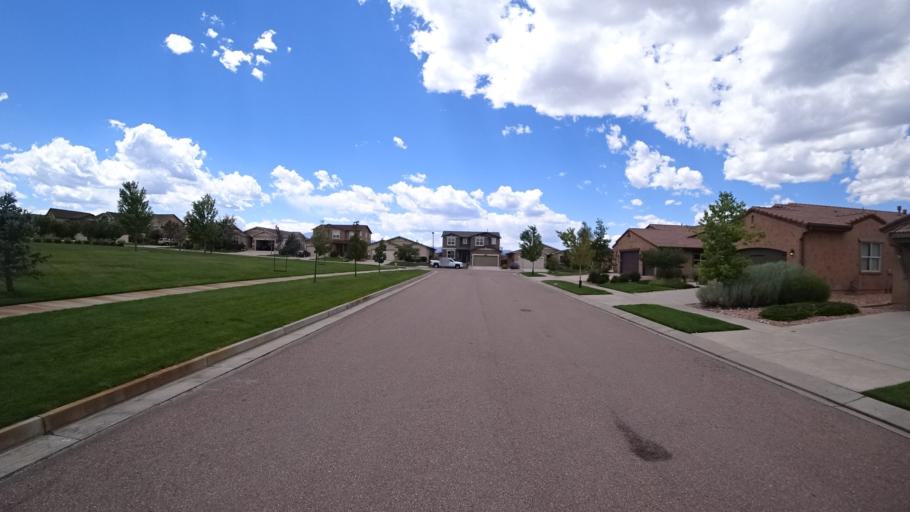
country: US
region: Colorado
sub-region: El Paso County
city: Black Forest
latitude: 38.9483
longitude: -104.7113
